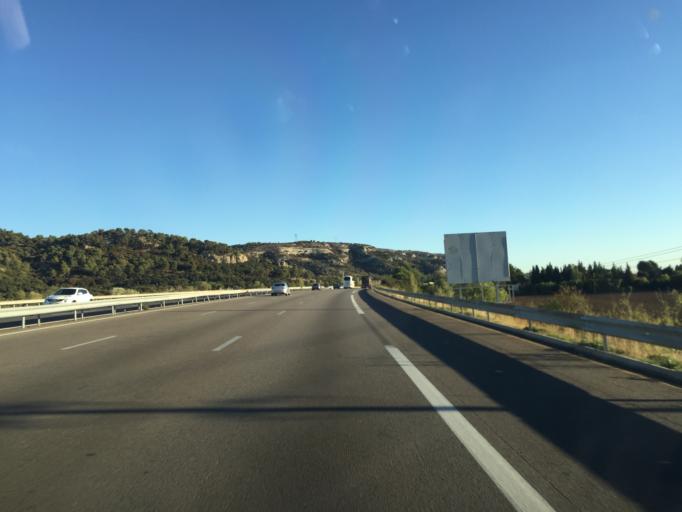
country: FR
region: Provence-Alpes-Cote d'Azur
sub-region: Departement des Bouches-du-Rhone
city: Lamanon
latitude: 43.7059
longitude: 5.0975
